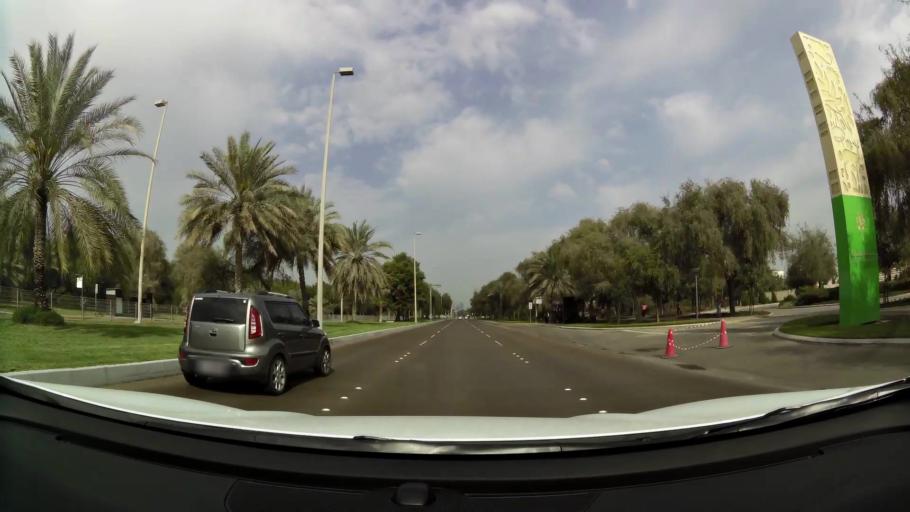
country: AE
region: Abu Dhabi
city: Abu Dhabi
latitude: 24.4496
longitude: 54.3815
